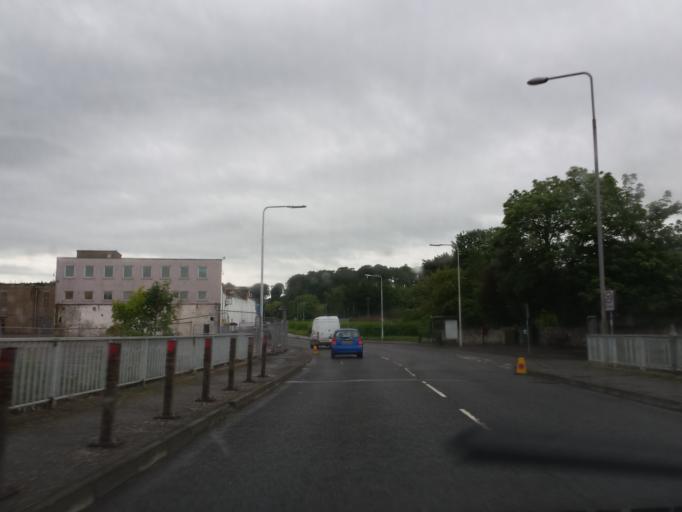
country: GB
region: Scotland
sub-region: Fife
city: Leuchars
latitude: 56.3670
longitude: -2.8916
